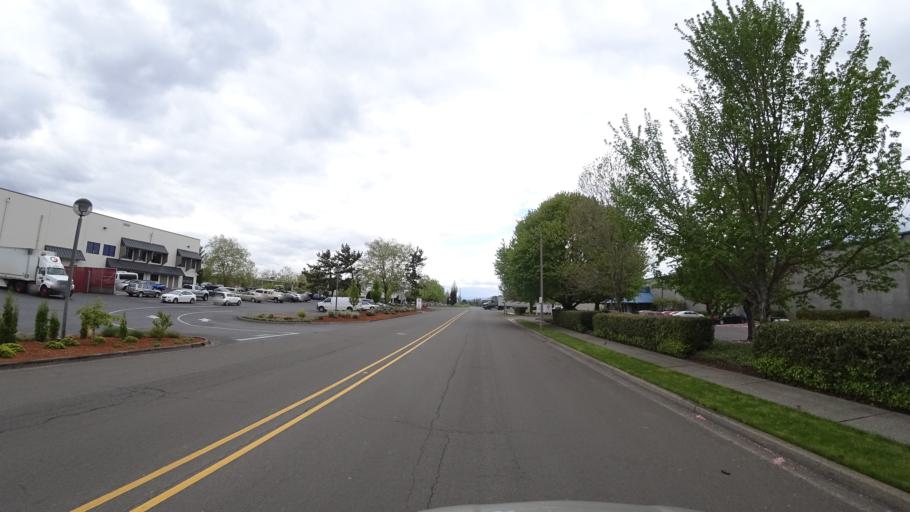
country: US
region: Oregon
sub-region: Washington County
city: Rockcreek
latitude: 45.5616
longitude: -122.9085
